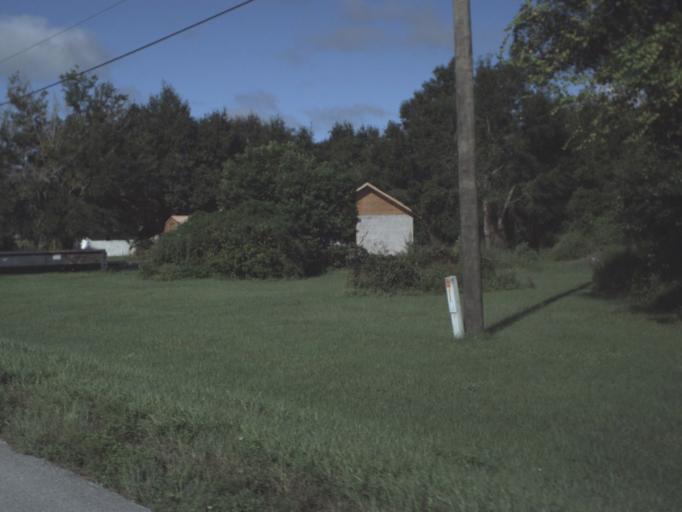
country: US
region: Florida
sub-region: DeSoto County
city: Arcadia
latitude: 27.2178
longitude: -81.9019
